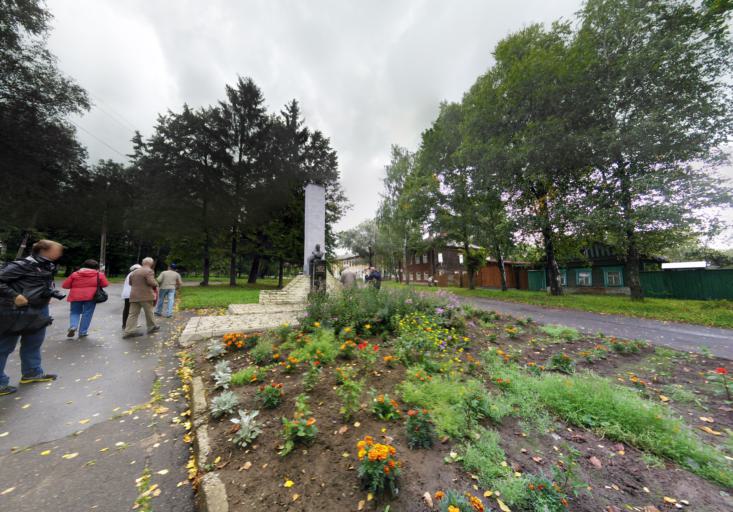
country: RU
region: Jaroslavl
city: Tutayev
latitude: 57.8802
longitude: 39.5407
